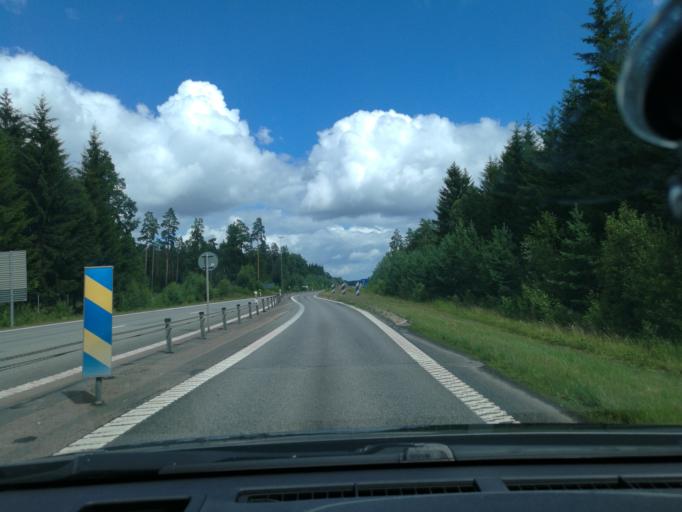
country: SE
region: Skane
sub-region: Hassleholms Kommun
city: Hassleholm
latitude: 56.1977
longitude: 13.8543
